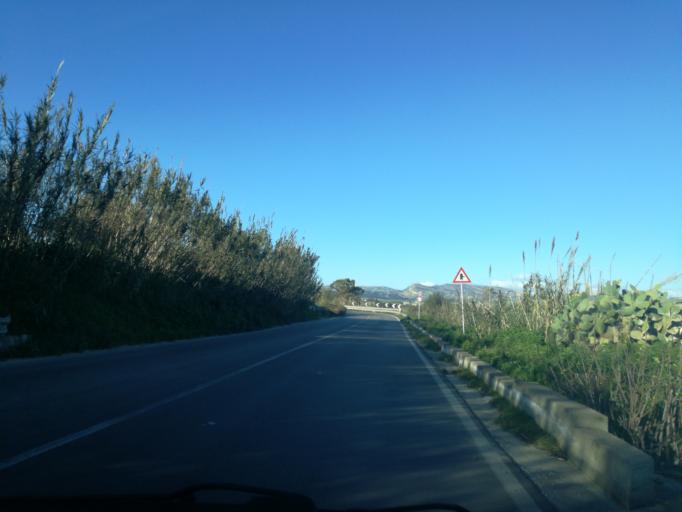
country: IT
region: Sicily
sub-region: Provincia di Caltanissetta
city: Butera
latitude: 37.1119
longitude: 14.1548
